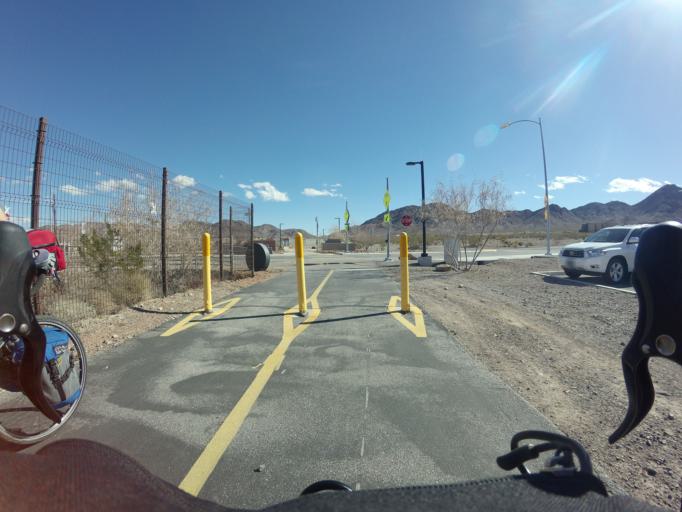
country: US
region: Nevada
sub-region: Clark County
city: Henderson
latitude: 35.9891
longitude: -114.9377
